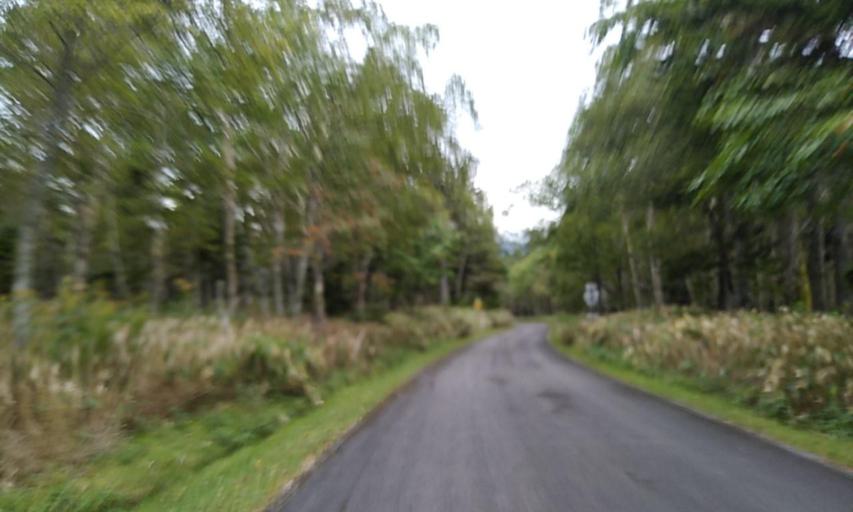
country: JP
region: Hokkaido
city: Bihoro
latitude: 43.5683
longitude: 144.2198
